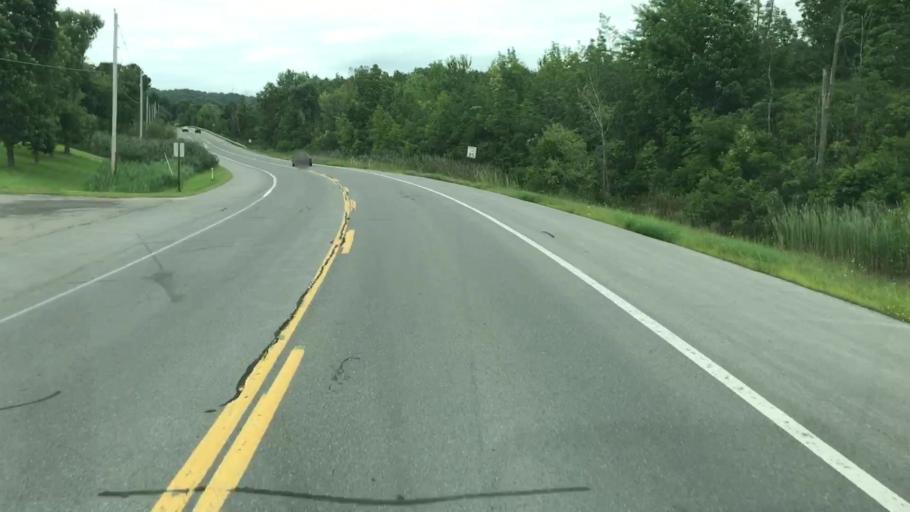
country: US
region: New York
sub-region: Onondaga County
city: Camillus
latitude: 43.0508
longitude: -76.3063
